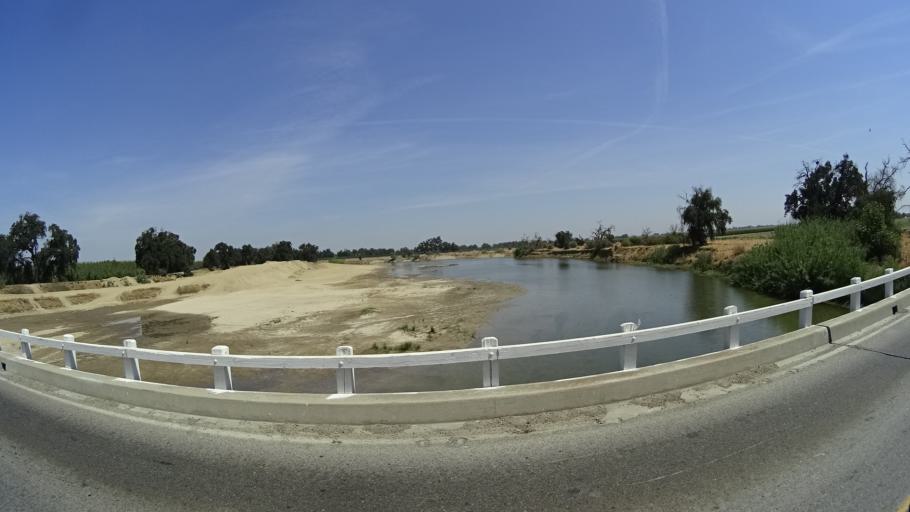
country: US
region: California
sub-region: Fresno County
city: Laton
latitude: 36.4014
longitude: -119.7516
